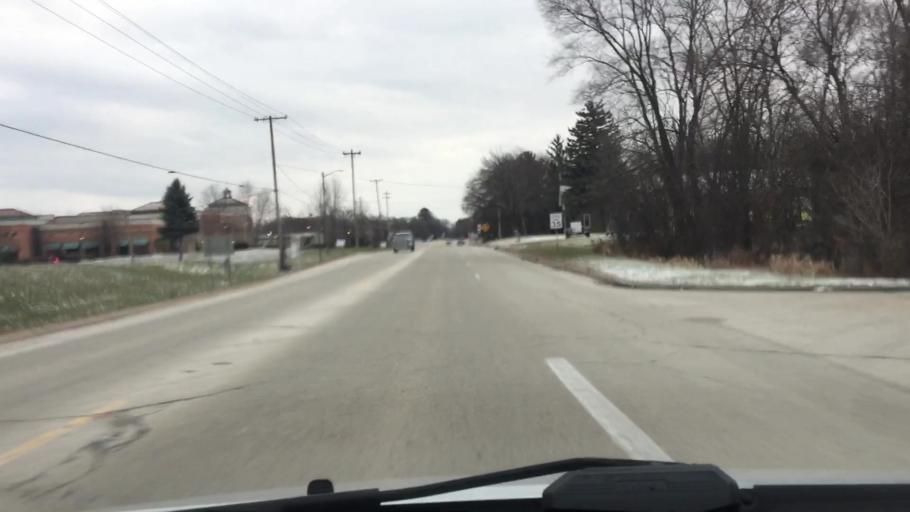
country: US
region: Wisconsin
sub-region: Waukesha County
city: Okauchee Lake
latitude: 43.1119
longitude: -88.4613
